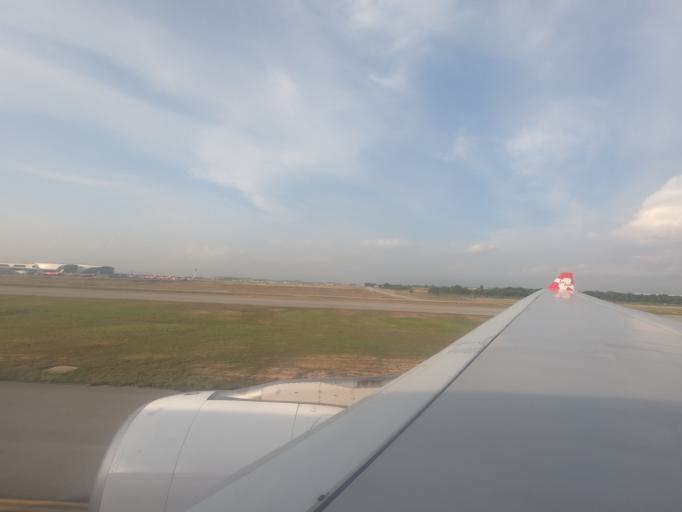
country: MY
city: Sungai Pelek New Village
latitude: 2.7294
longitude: 101.6855
